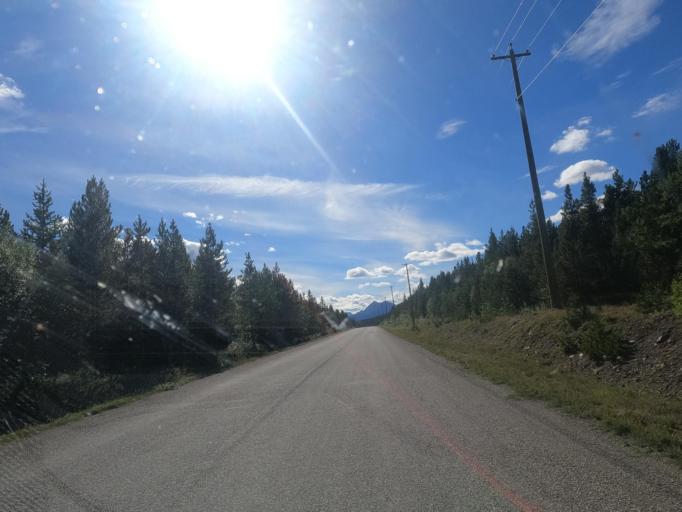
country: CA
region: Yukon
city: Watson Lake
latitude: 59.2750
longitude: -129.5579
